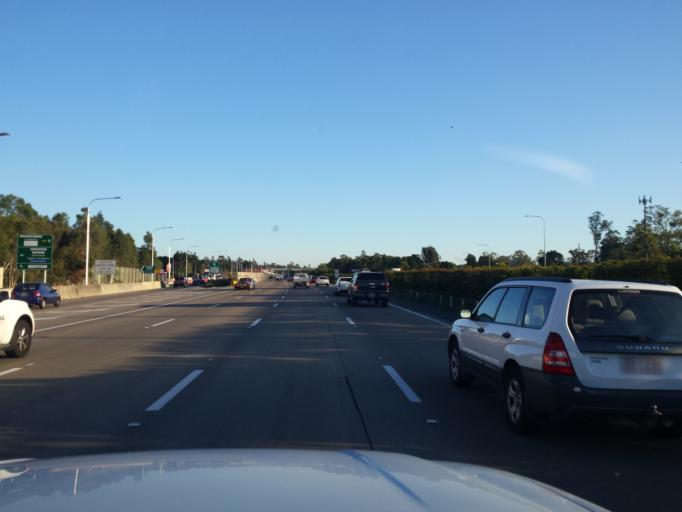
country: AU
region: Queensland
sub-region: Gold Coast
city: Oxenford
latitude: -27.8649
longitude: 153.3119
